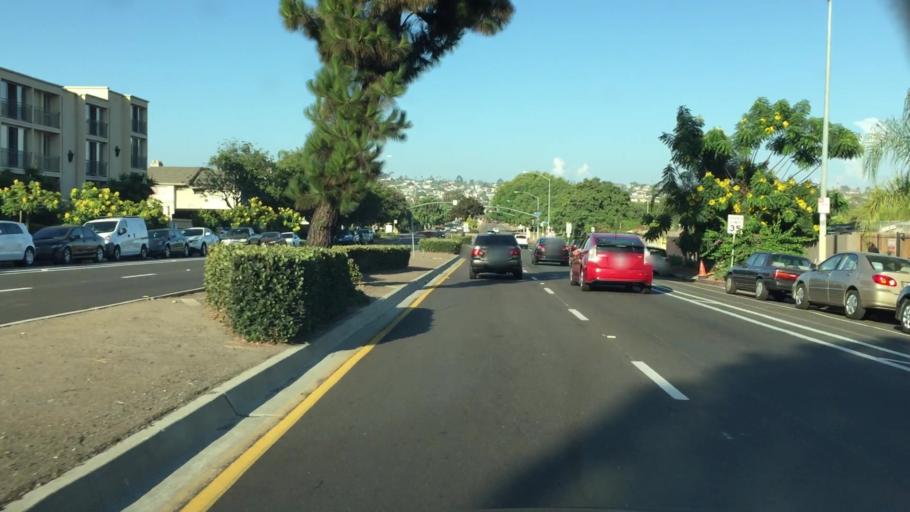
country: US
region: California
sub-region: San Diego County
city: La Jolla
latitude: 32.8006
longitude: -117.2276
